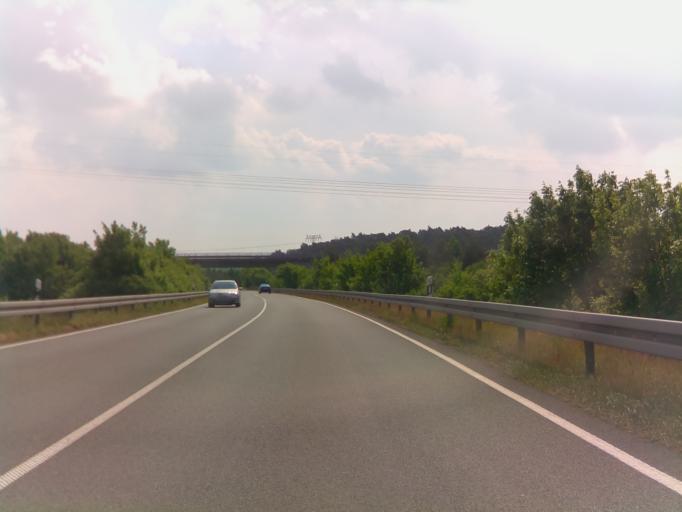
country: DE
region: Saxony-Anhalt
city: Stendal
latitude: 52.5741
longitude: 11.8388
